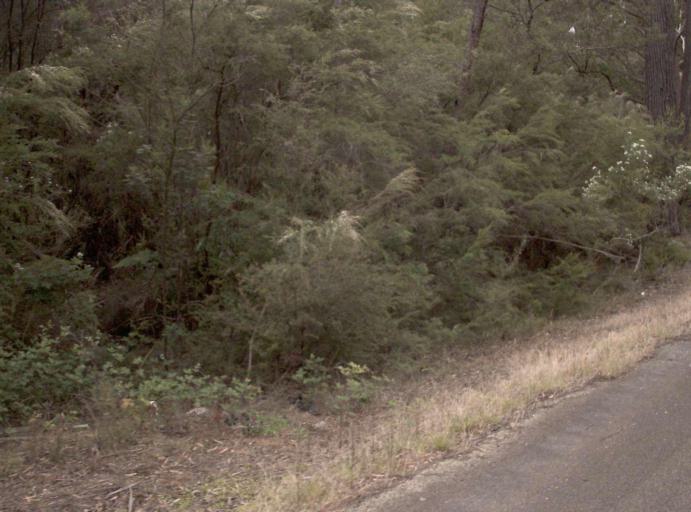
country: AU
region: Victoria
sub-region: East Gippsland
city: Lakes Entrance
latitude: -37.7291
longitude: 147.9198
